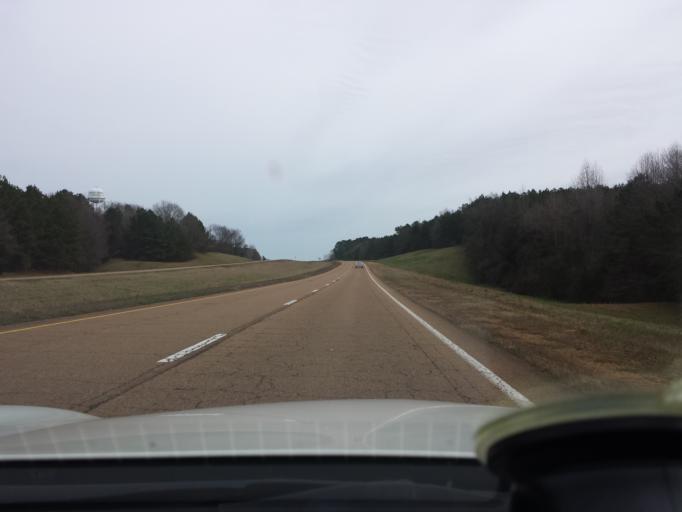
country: US
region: Mississippi
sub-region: Leake County
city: Carthage
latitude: 32.8734
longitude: -89.4151
